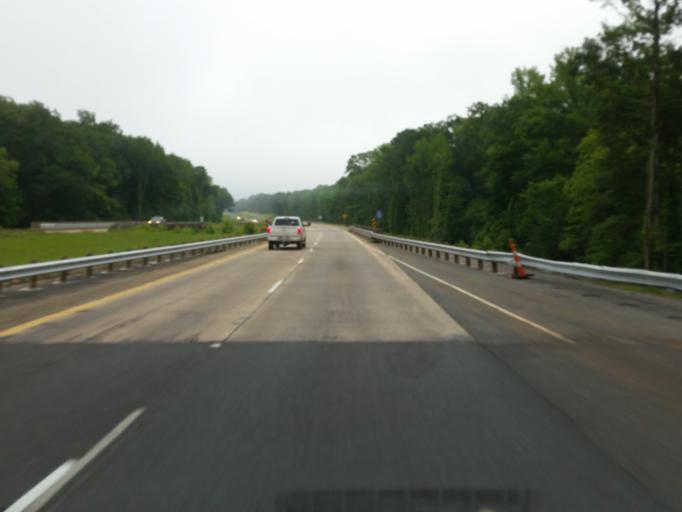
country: US
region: Louisiana
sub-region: Webster Parish
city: Minden
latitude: 32.5620
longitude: -93.1538
